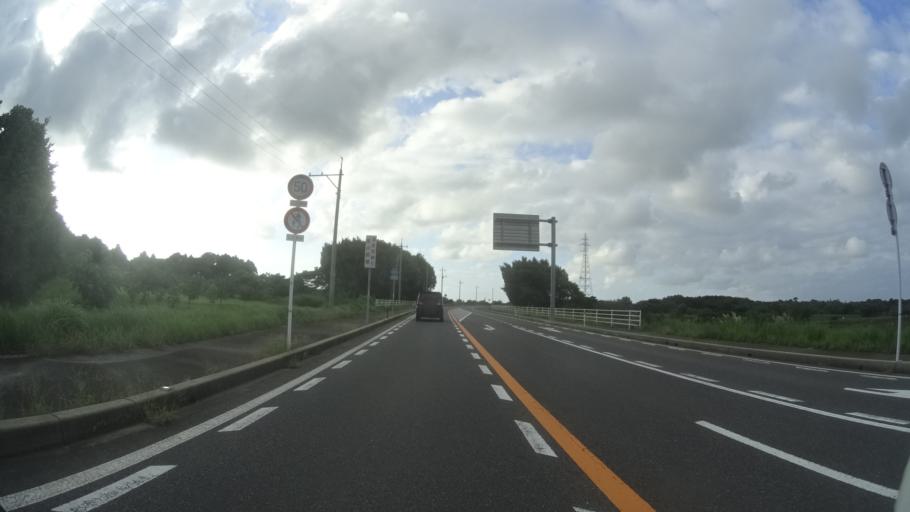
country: JP
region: Tottori
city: Kurayoshi
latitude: 35.5134
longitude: 133.6000
